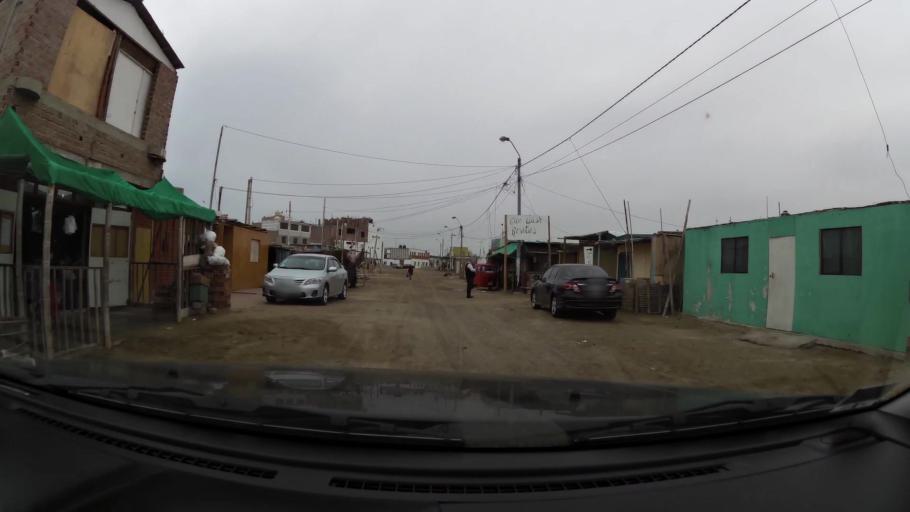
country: PE
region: Ica
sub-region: Provincia de Pisco
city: Paracas
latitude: -13.8354
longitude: -76.2484
